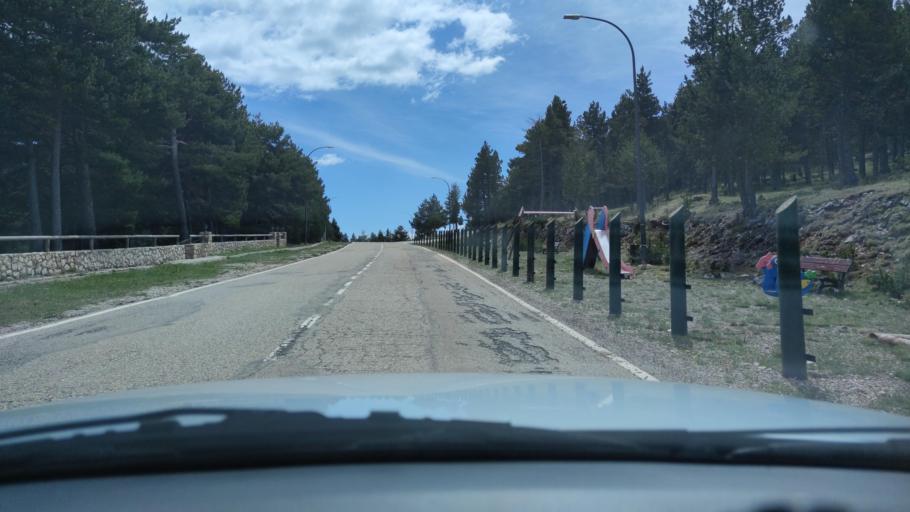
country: ES
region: Catalonia
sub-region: Provincia de Lleida
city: Gosol
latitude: 42.1763
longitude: 1.5623
